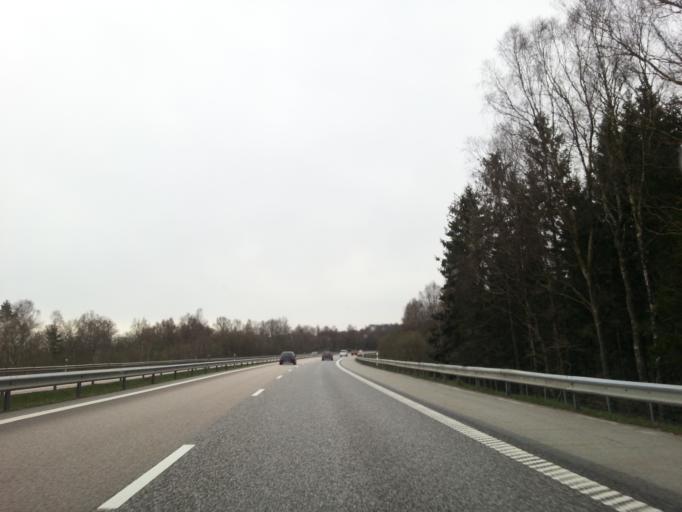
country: SE
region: Skane
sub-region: Bastads Kommun
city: Bastad
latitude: 56.3597
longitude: 12.9351
